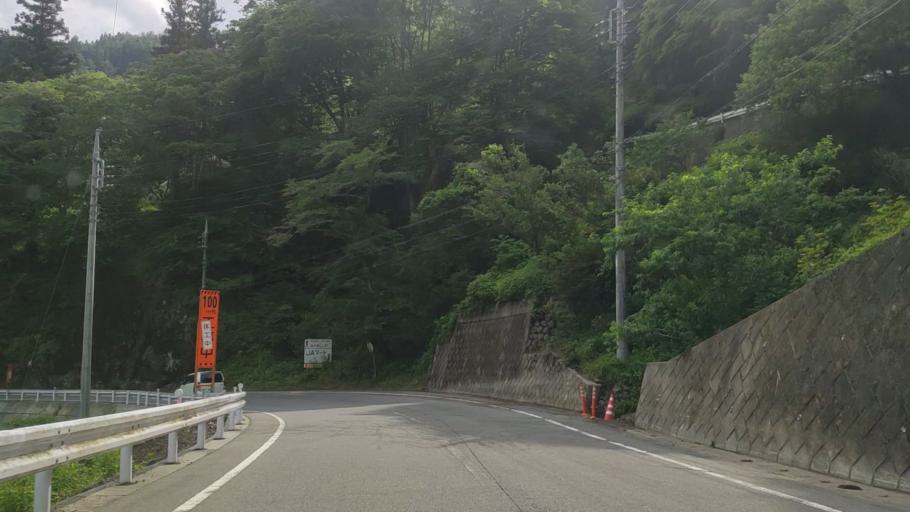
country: JP
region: Gunma
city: Tomioka
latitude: 36.1074
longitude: 138.7171
